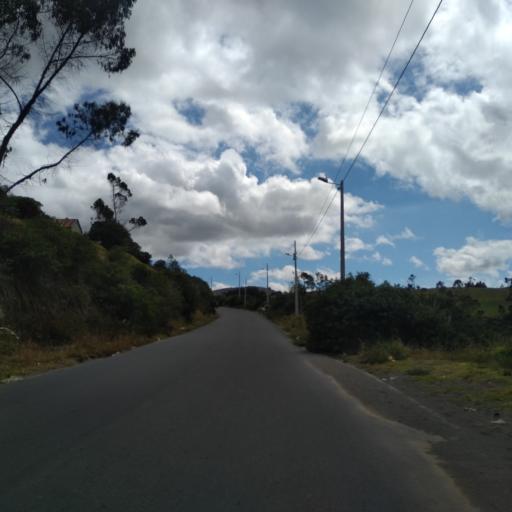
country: EC
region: Cotopaxi
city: Saquisili
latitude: -0.7523
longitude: -78.7272
